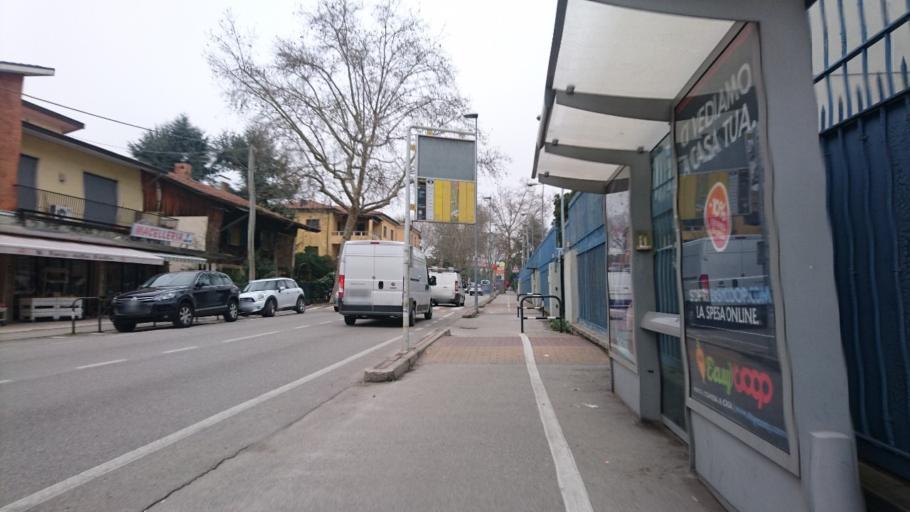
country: IT
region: Veneto
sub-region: Provincia di Padova
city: Padova
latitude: 45.3915
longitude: 11.8792
